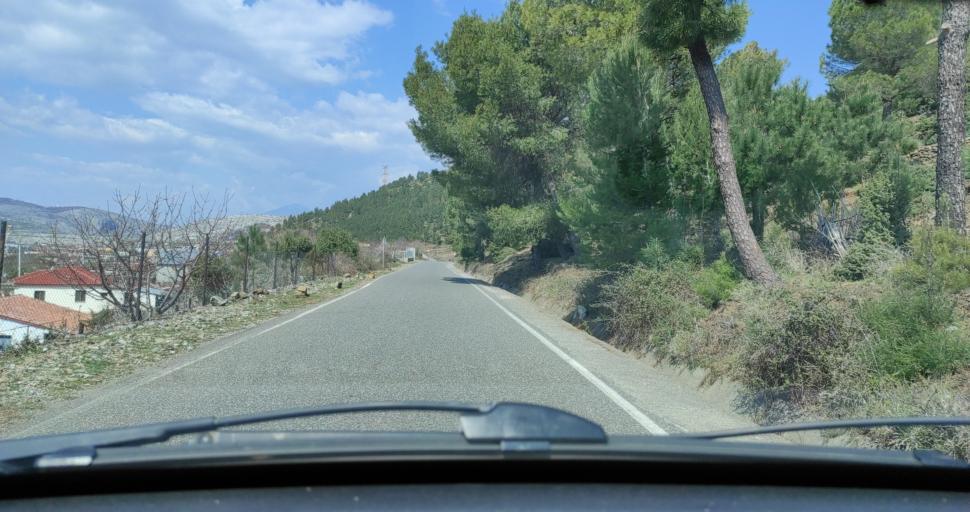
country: AL
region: Shkoder
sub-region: Rrethi i Shkodres
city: Vau i Dejes
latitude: 41.9972
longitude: 19.6496
